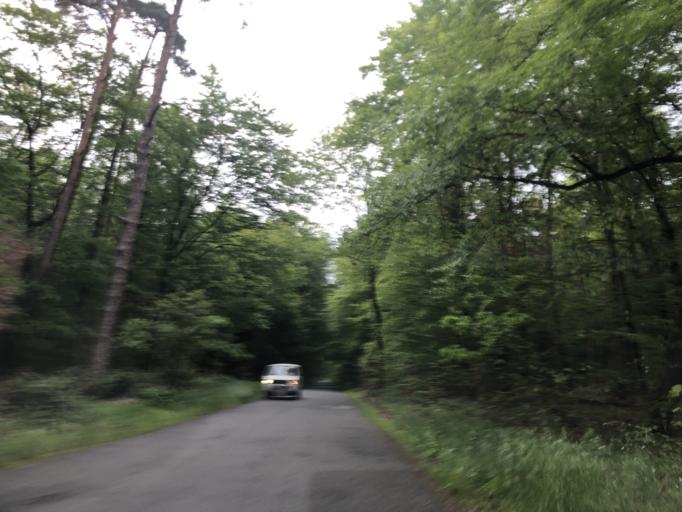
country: DE
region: Hesse
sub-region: Regierungsbezirk Darmstadt
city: Erzhausen
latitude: 49.9500
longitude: 8.6050
